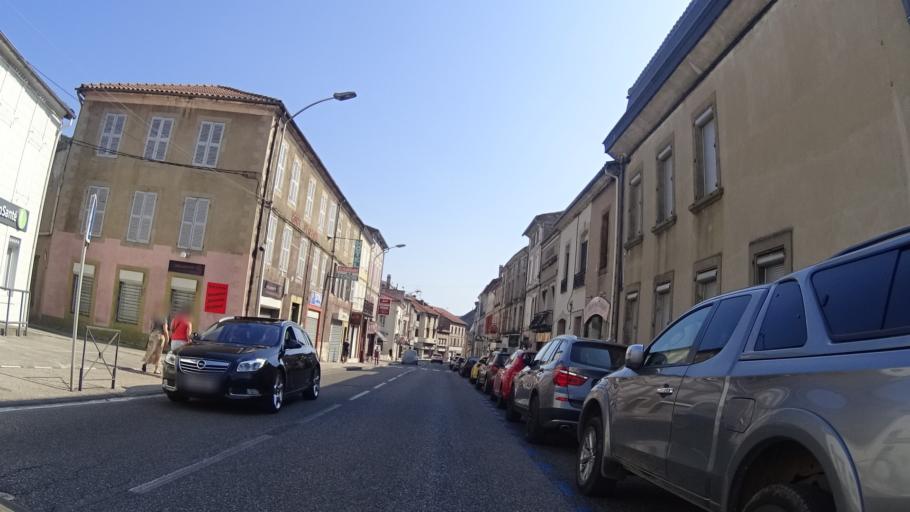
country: FR
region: Midi-Pyrenees
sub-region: Departement de l'Ariege
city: Lavelanet
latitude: 42.9317
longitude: 1.8466
